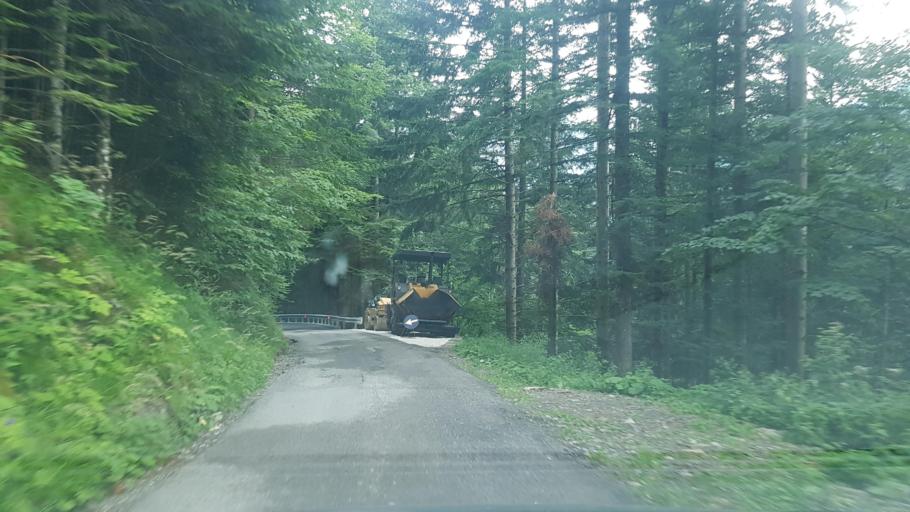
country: IT
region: Friuli Venezia Giulia
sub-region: Provincia di Udine
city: Paularo
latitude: 46.5466
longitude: 13.1224
